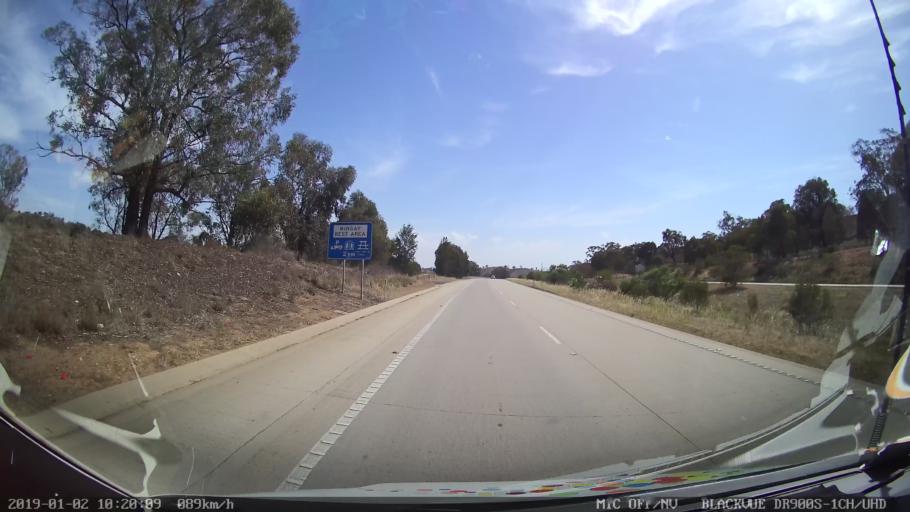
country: AU
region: New South Wales
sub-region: Gundagai
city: Gundagai
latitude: -34.9894
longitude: 148.1160
